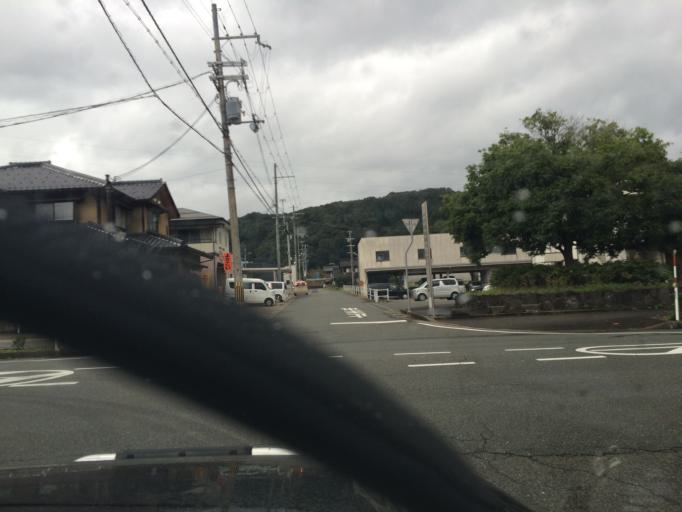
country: JP
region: Hyogo
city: Toyooka
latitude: 35.4693
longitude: 134.7694
